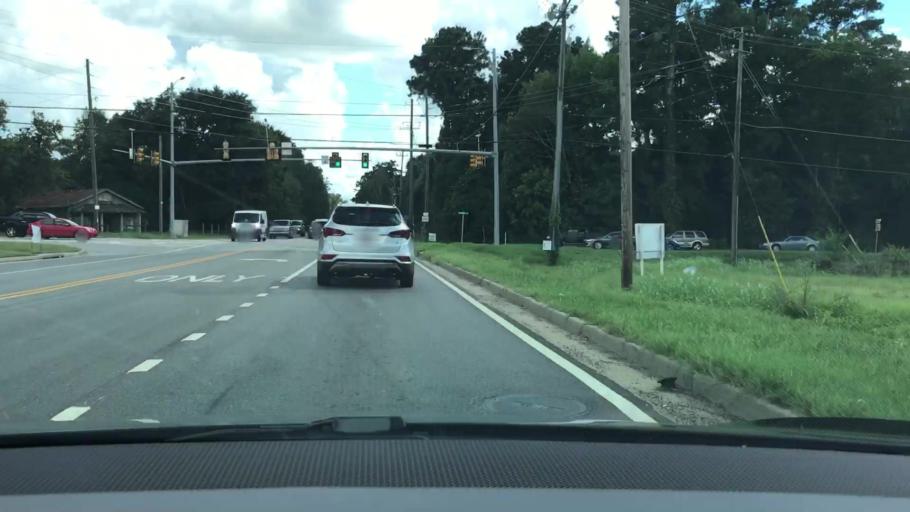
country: US
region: Alabama
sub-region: Montgomery County
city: Pike Road
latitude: 32.3474
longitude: -86.0951
